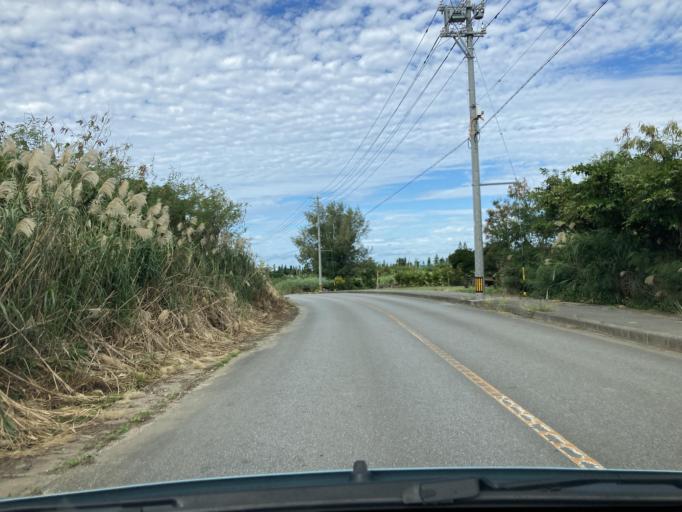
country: JP
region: Okinawa
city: Ishikawa
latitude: 26.4325
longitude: 127.7269
